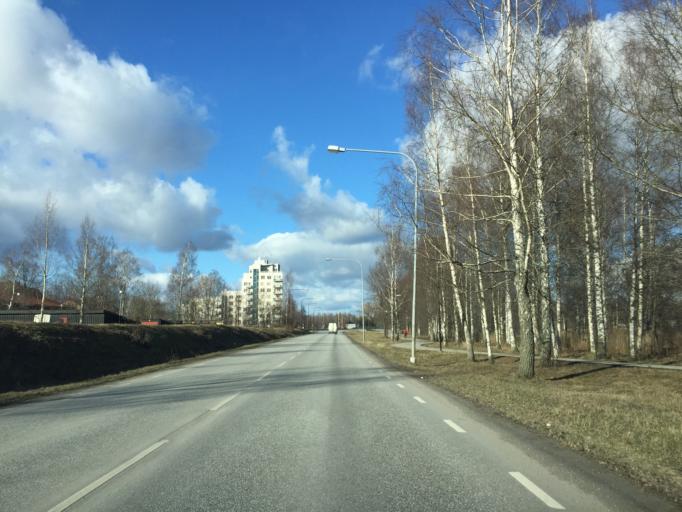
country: SE
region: OErebro
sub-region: Orebro Kommun
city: Orebro
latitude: 59.2700
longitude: 15.2410
